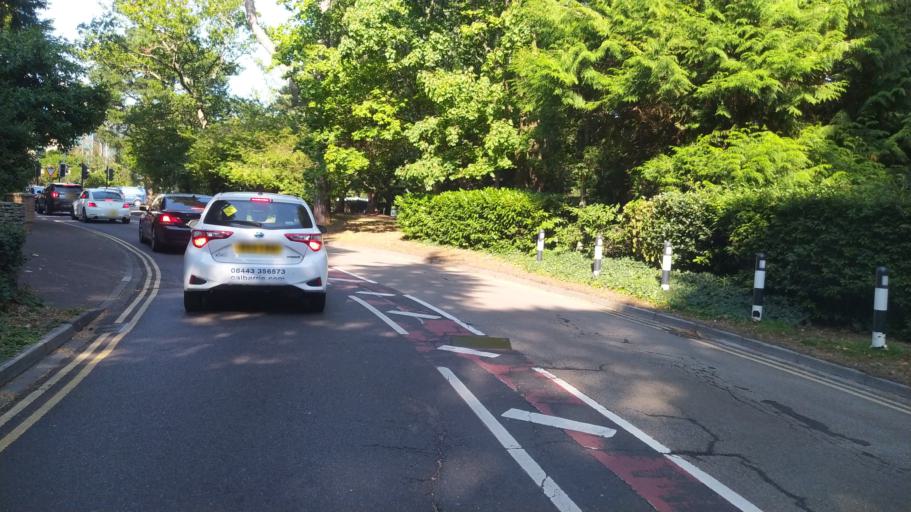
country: GB
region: England
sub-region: Bournemouth
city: Bournemouth
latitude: 50.7223
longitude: -1.9071
